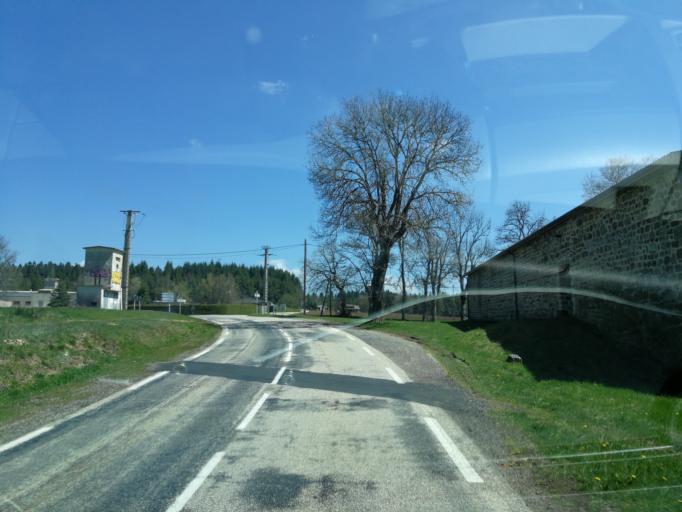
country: FR
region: Rhone-Alpes
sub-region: Departement de l'Ardeche
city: Saint-Agreve
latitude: 45.0182
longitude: 4.4063
